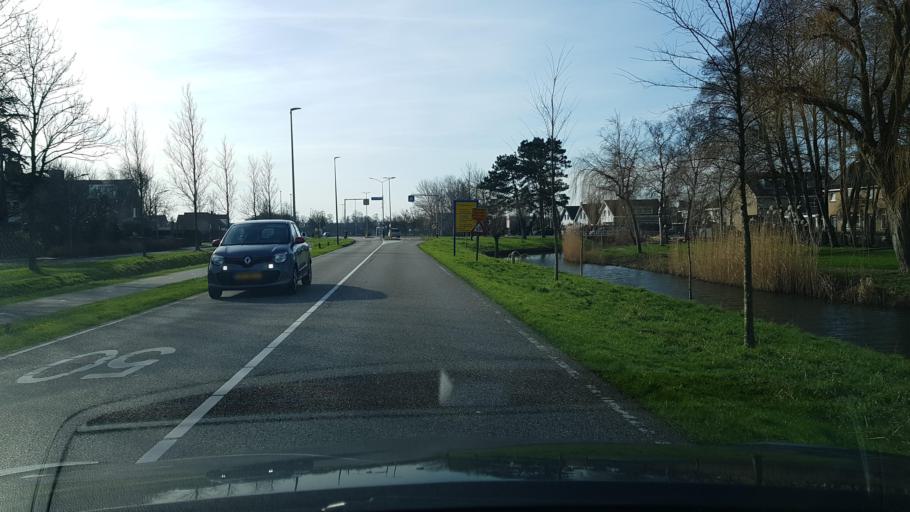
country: NL
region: North Holland
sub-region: Gemeente Uitgeest
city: Uitgeest
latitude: 52.5274
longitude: 4.7064
